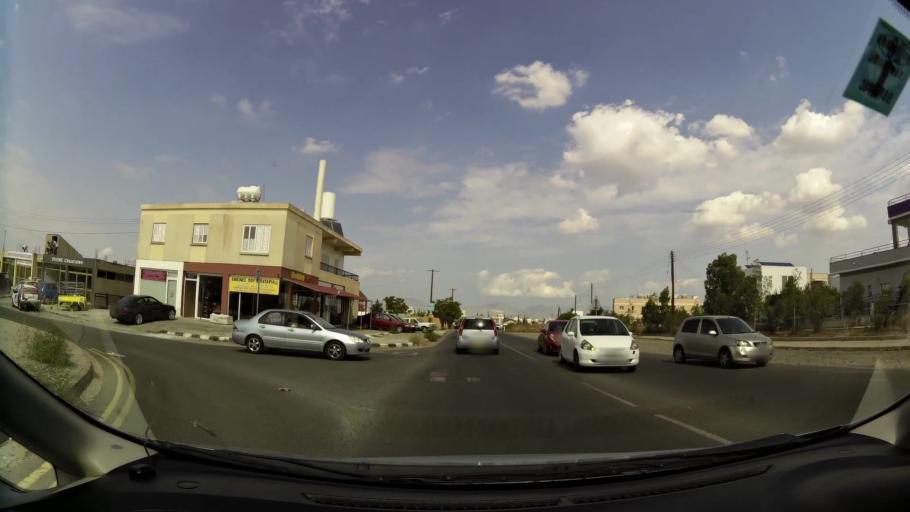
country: CY
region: Lefkosia
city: Tseri
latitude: 35.1159
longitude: 33.3326
